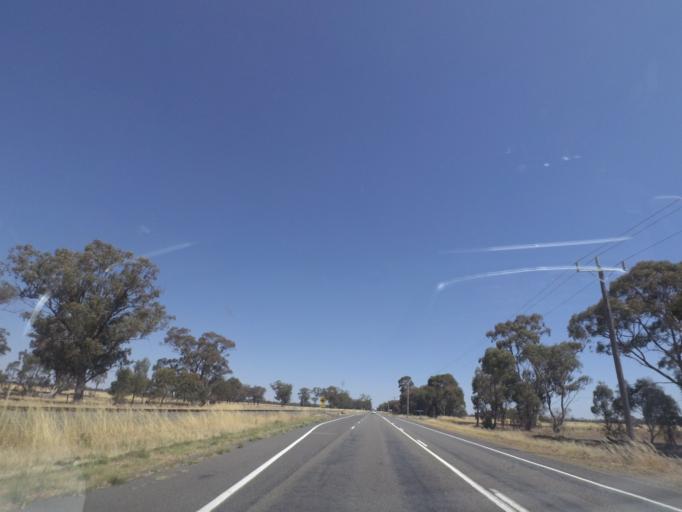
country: AU
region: Victoria
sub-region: Greater Shepparton
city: Shepparton
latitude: -36.1982
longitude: 145.4318
